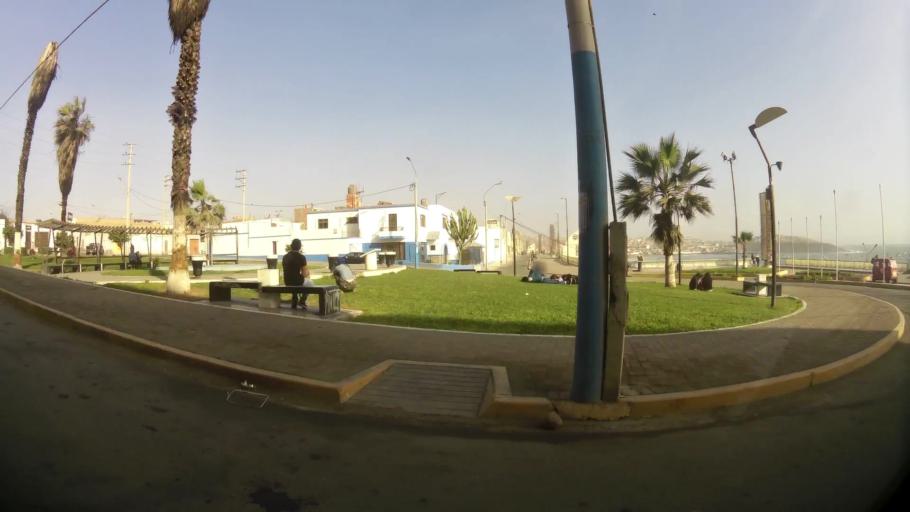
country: PE
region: Lima
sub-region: Huaura
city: Huacho
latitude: -11.1103
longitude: -77.6134
